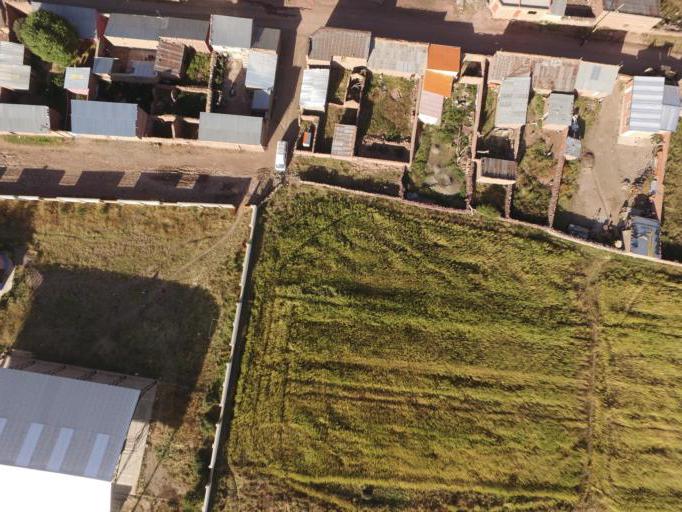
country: BO
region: Oruro
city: Challapata
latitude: -18.6938
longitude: -66.7570
